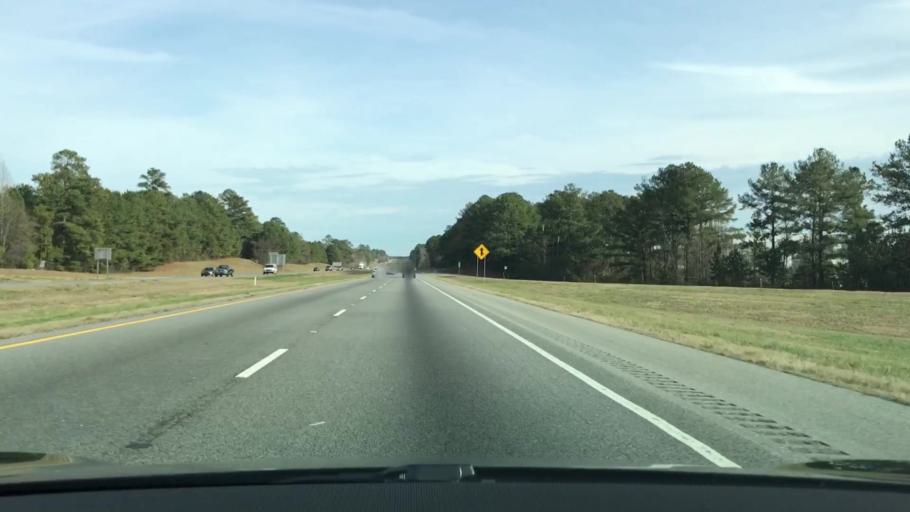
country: US
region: Georgia
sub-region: Walton County
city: Social Circle
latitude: 33.6089
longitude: -83.6967
